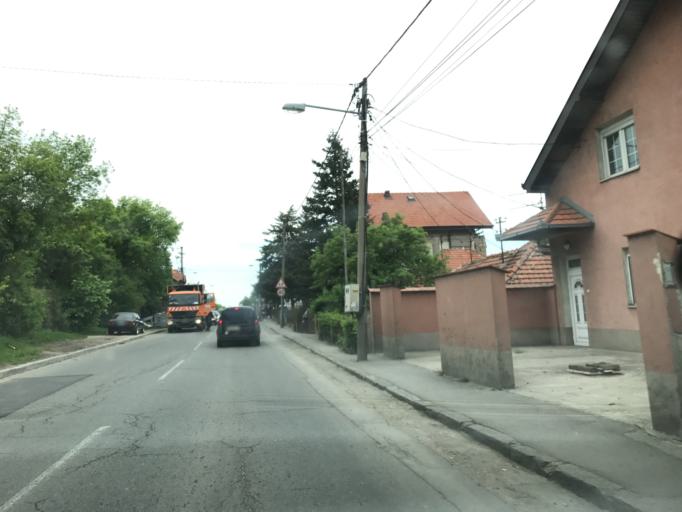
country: RS
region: Central Serbia
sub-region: Belgrade
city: Palilula
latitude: 44.8071
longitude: 20.5154
